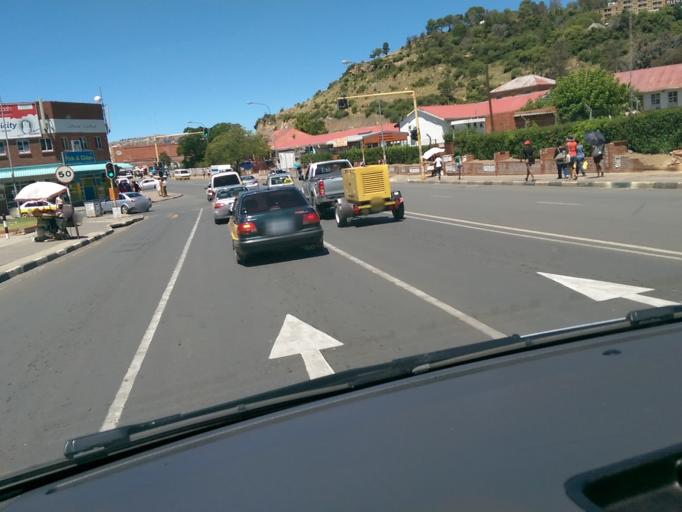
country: LS
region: Maseru
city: Maseru
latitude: -29.3149
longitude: 27.4864
